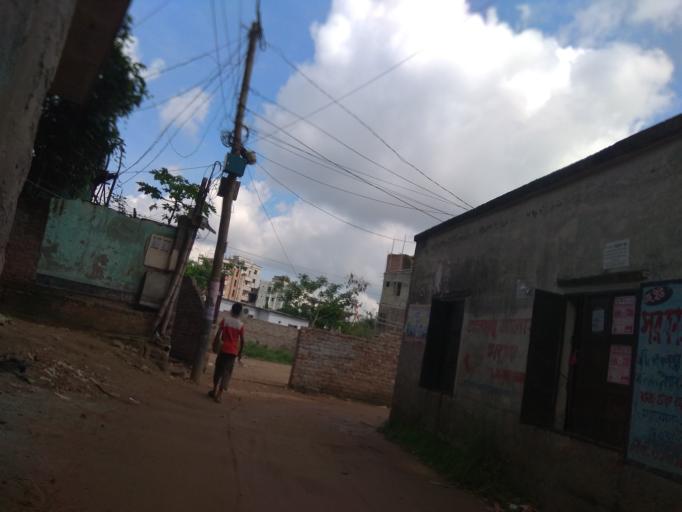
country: BD
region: Dhaka
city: Tungi
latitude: 23.8155
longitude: 90.3898
